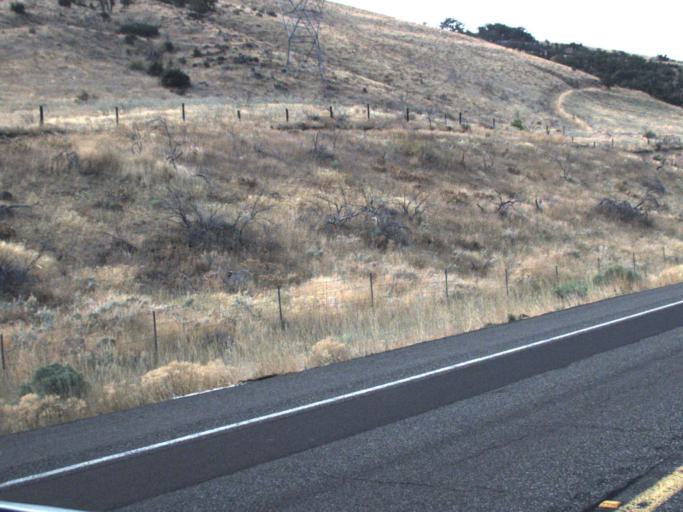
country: US
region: Washington
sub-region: Klickitat County
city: Goldendale
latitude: 46.0779
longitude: -120.5553
